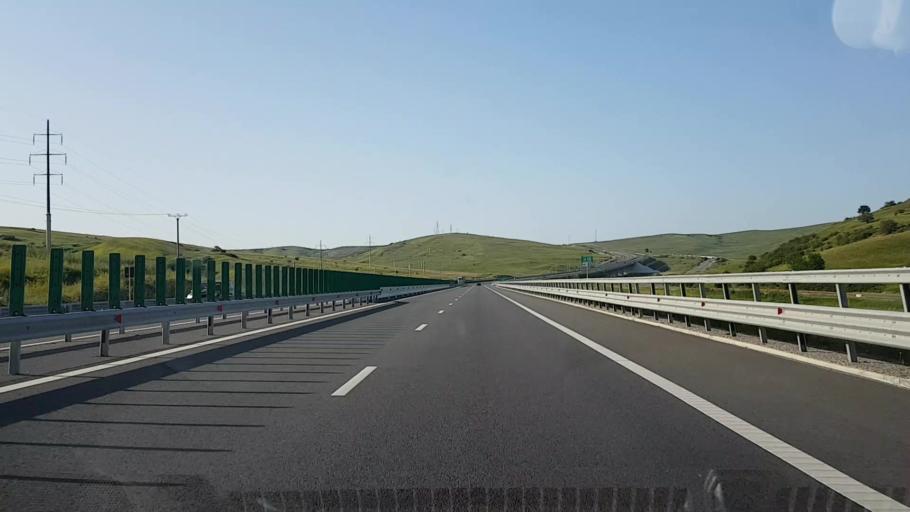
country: RO
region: Cluj
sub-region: Comuna Mihai Viteazu
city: Mihai Viteazu
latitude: 46.4805
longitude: 23.7762
